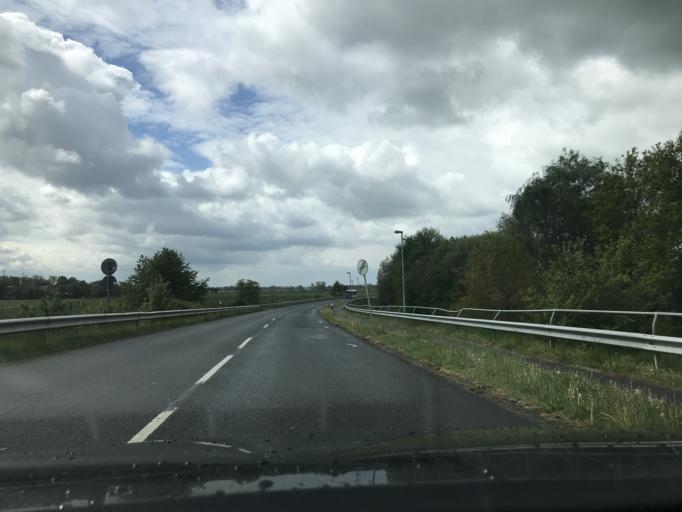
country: DE
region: Lower Saxony
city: Lemwerder
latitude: 53.1657
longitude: 8.5857
